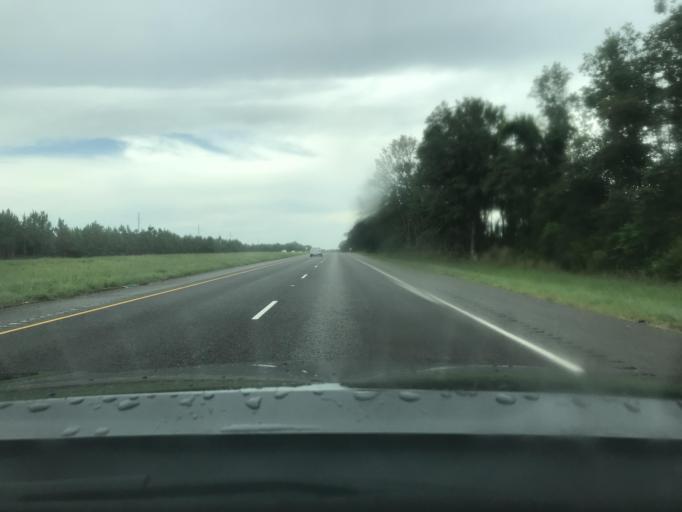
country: US
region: Louisiana
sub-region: Calcasieu Parish
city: Moss Bluff
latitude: 30.3912
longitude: -93.2231
